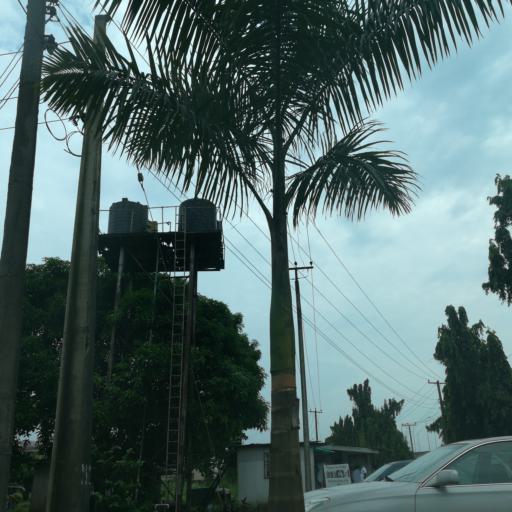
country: NG
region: Rivers
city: Port Harcourt
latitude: 4.8170
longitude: 6.9837
